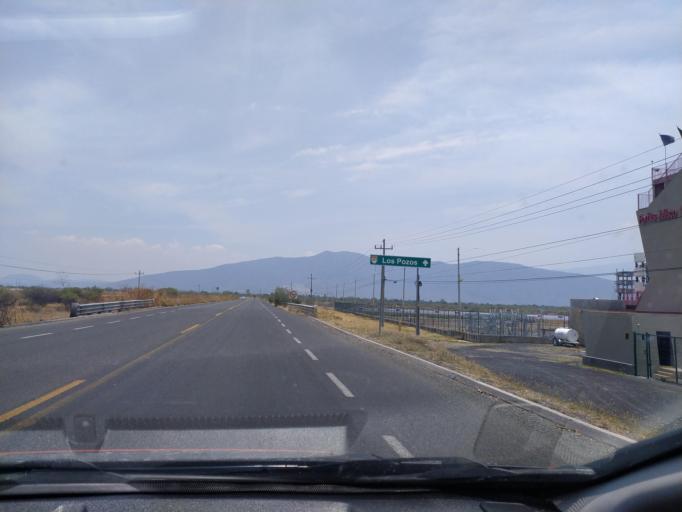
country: MX
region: Jalisco
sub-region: Zacoalco de Torres
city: Barranca de Otates (Barranca de Otatan)
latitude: 20.3118
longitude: -103.5925
